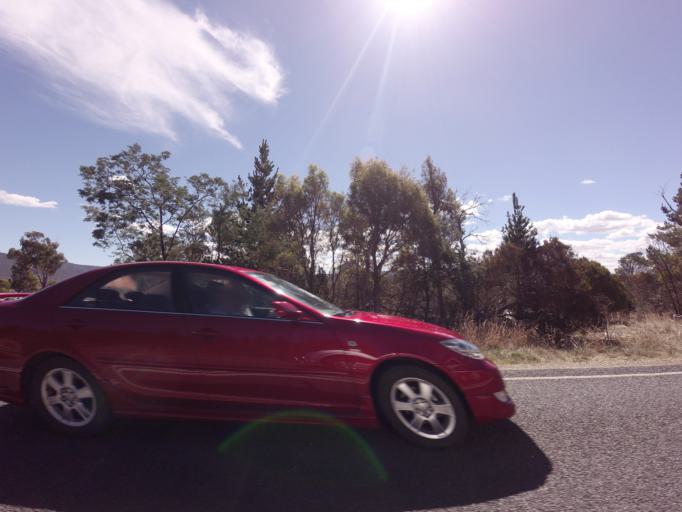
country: AU
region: Tasmania
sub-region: Break O'Day
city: St Helens
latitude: -41.6825
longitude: 147.8867
